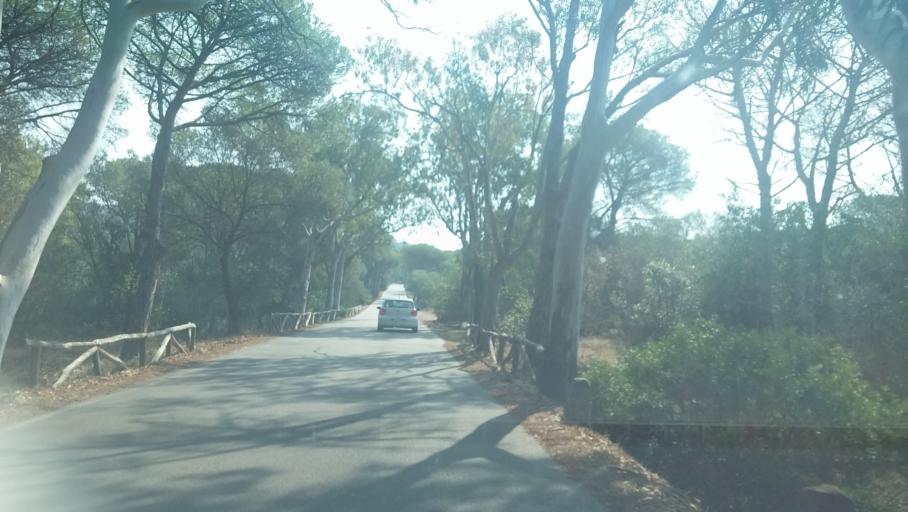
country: IT
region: Sardinia
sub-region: Provincia di Olbia-Tempio
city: La Maddalena
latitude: 41.2105
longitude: 9.4567
